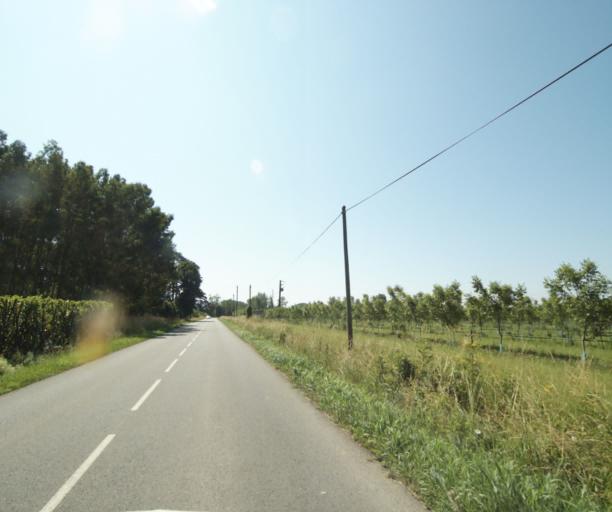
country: FR
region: Midi-Pyrenees
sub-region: Departement du Tarn-et-Garonne
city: Montbeton
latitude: 44.0422
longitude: 1.2950
